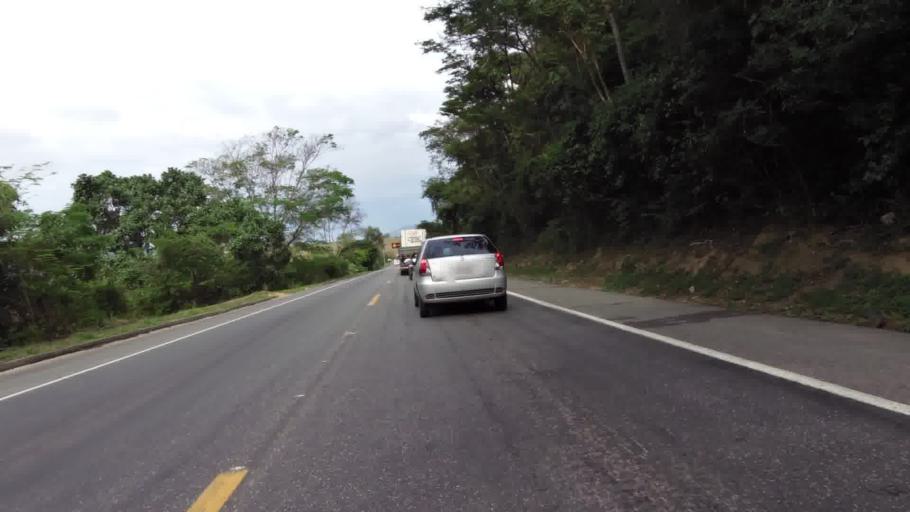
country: BR
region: Espirito Santo
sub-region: Alfredo Chaves
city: Alfredo Chaves
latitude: -20.7130
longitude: -40.7254
